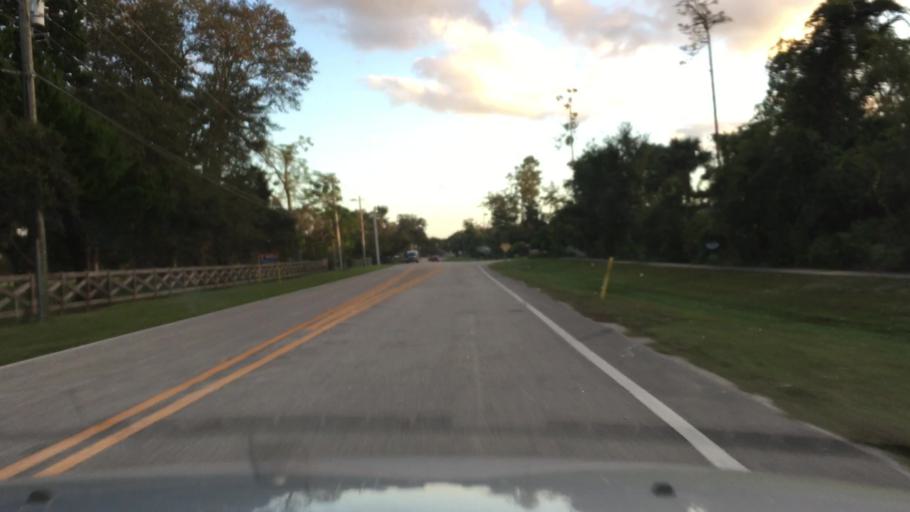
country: US
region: Florida
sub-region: Volusia County
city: Ormond Beach
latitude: 29.2809
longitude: -81.1130
